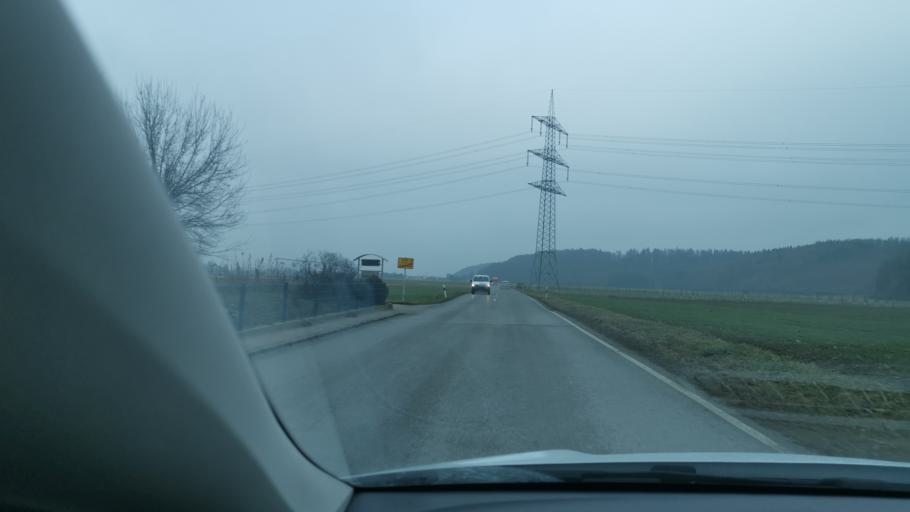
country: DE
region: Bavaria
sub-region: Swabia
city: Todtenweis
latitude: 48.4993
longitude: 10.9209
